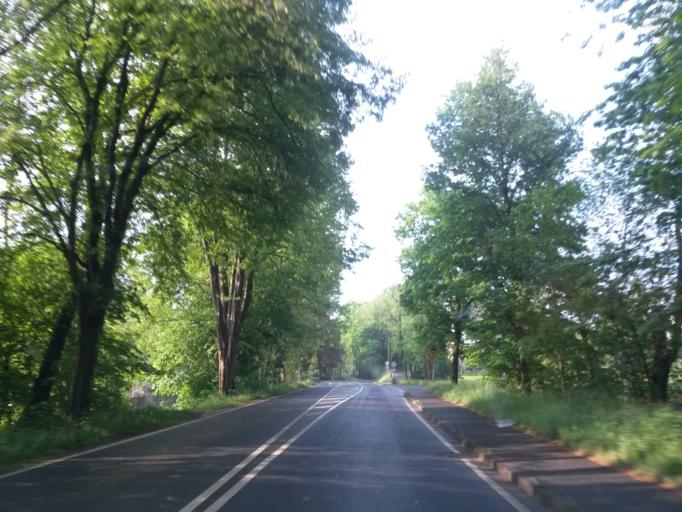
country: DE
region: North Rhine-Westphalia
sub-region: Regierungsbezirk Koln
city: Much
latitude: 50.8994
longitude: 7.4076
